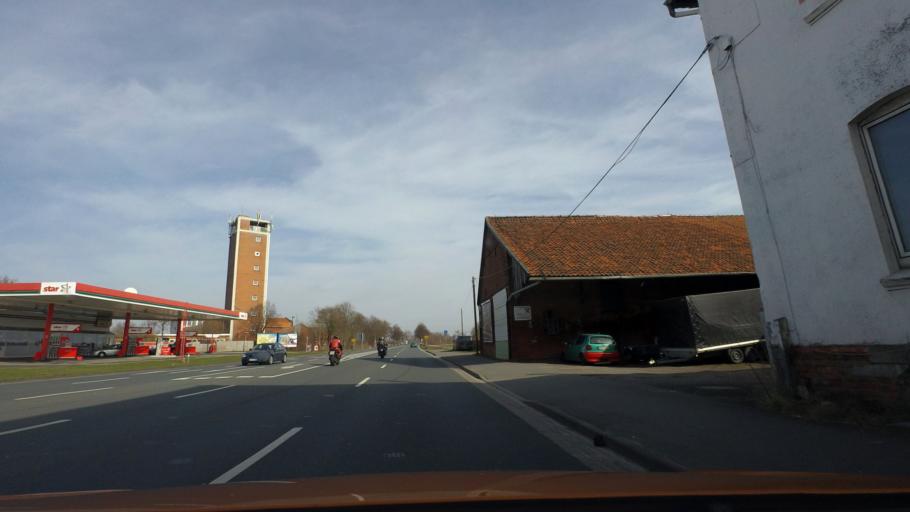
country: DE
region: Lower Saxony
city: Ronnenberg
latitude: 52.3190
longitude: 9.6676
